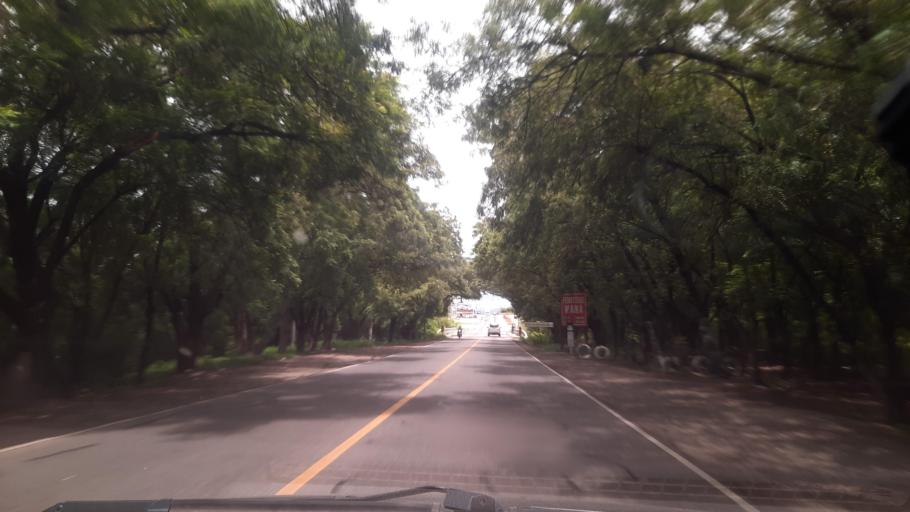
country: GT
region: Zacapa
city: Estanzuela
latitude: 15.0089
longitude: -89.5740
